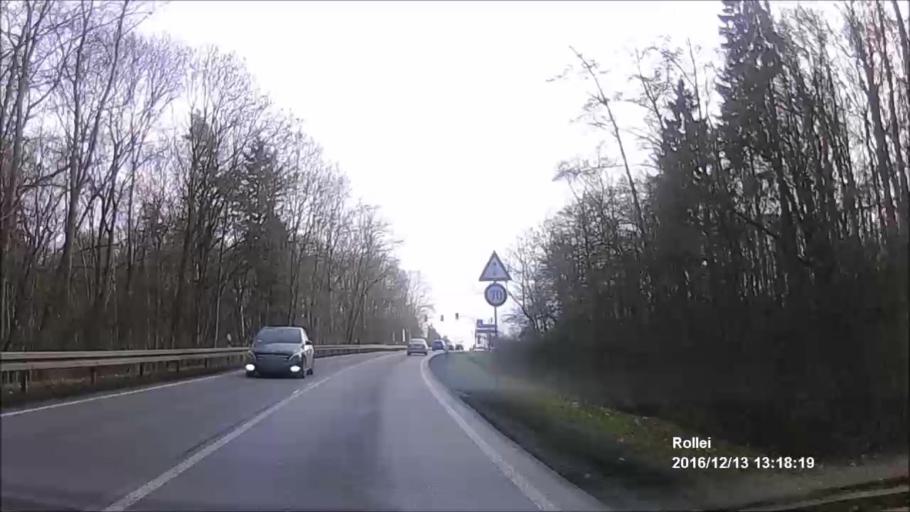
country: DE
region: Thuringia
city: Klettbach
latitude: 50.9289
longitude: 11.1364
